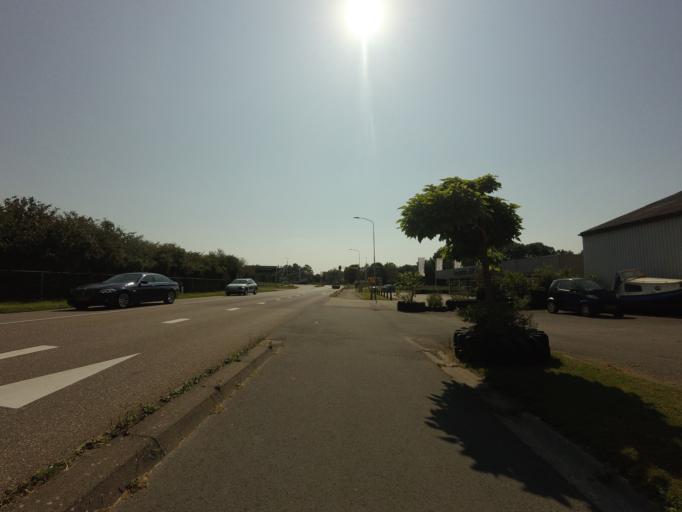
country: NL
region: Groningen
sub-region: Gemeente Zuidhorn
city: Grijpskerk
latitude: 53.2663
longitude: 6.3066
